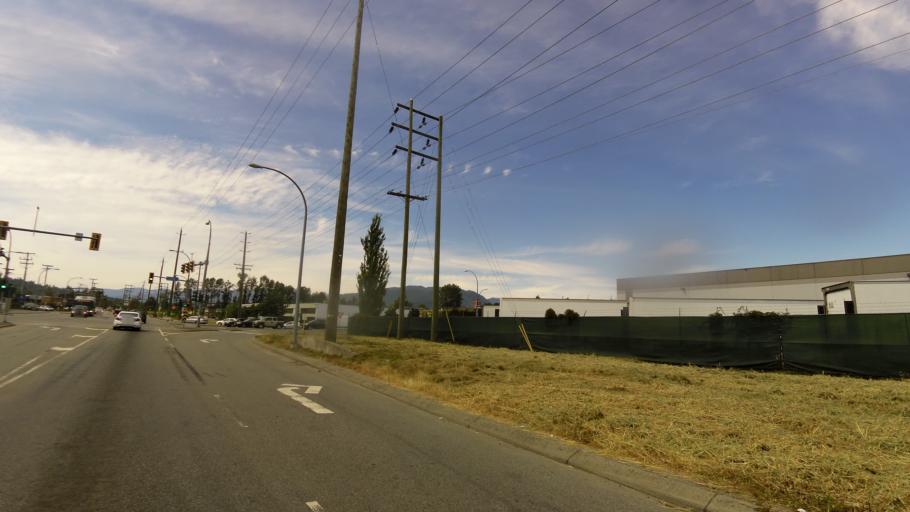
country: CA
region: British Columbia
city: Coquitlam
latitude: 49.2526
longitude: -122.7615
